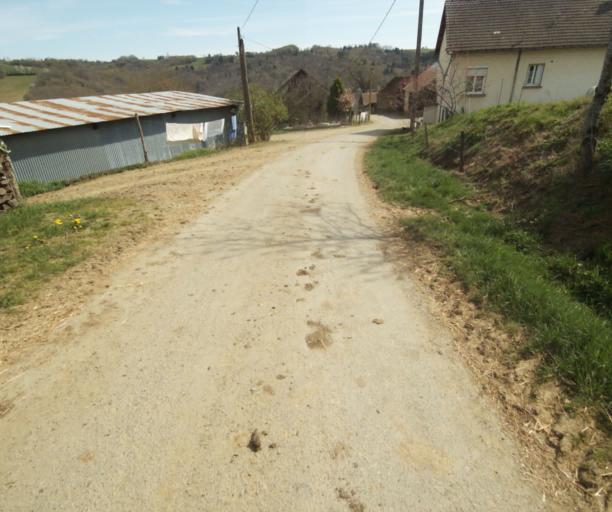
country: FR
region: Limousin
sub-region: Departement de la Correze
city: Naves
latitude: 45.3751
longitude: 1.7821
